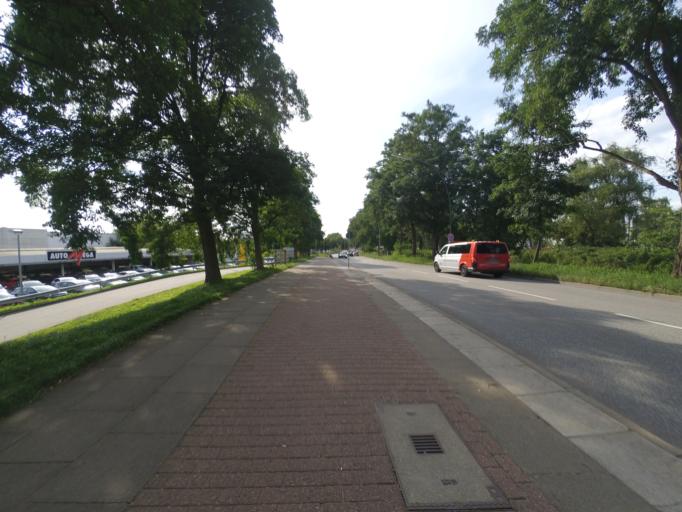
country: DE
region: Hamburg
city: Bergedorf
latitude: 53.4851
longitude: 10.2044
